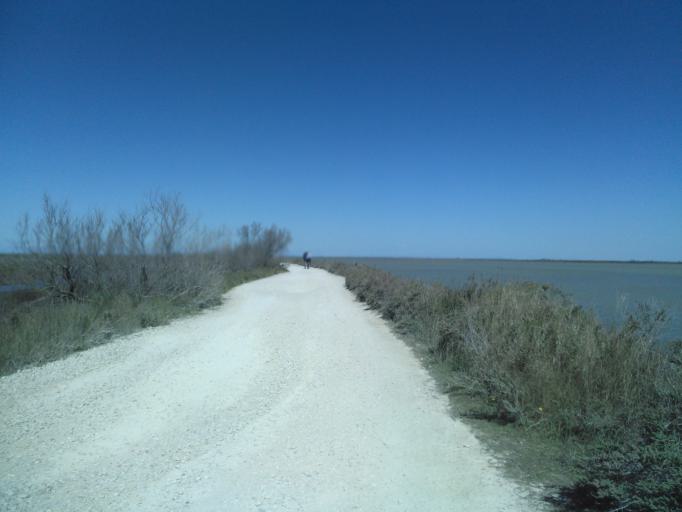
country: FR
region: Provence-Alpes-Cote d'Azur
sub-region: Departement des Bouches-du-Rhone
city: Saintes-Maries-de-la-Mer
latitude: 43.4421
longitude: 4.6114
